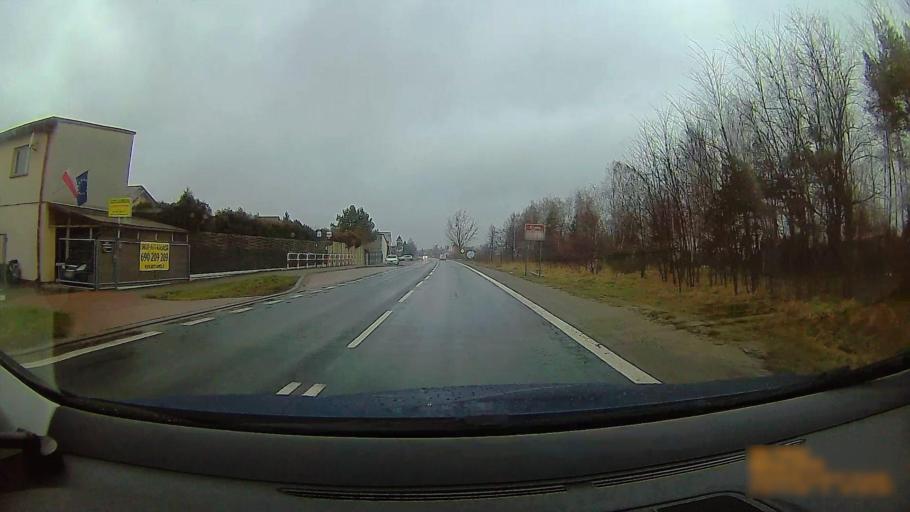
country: PL
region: Greater Poland Voivodeship
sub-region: Konin
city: Konin
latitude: 52.1835
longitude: 18.2689
